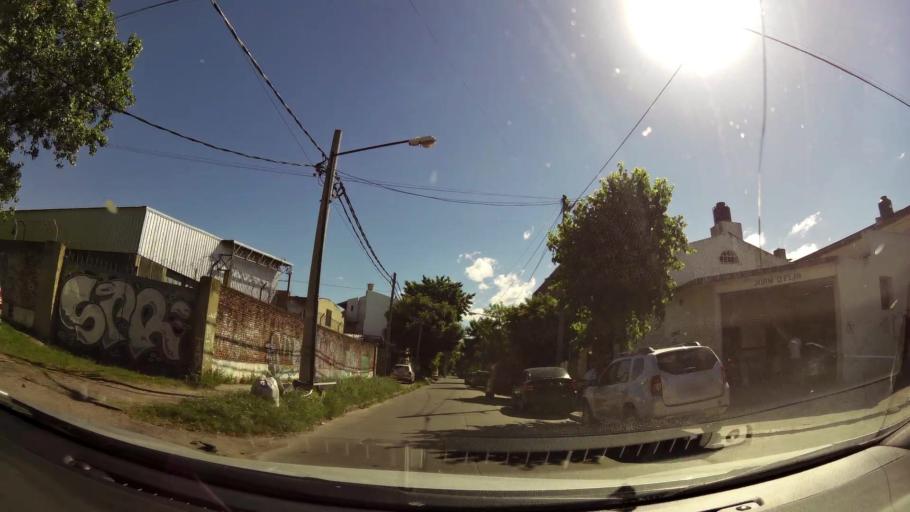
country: AR
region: Buenos Aires
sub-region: Partido de San Isidro
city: San Isidro
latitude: -34.4668
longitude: -58.5370
